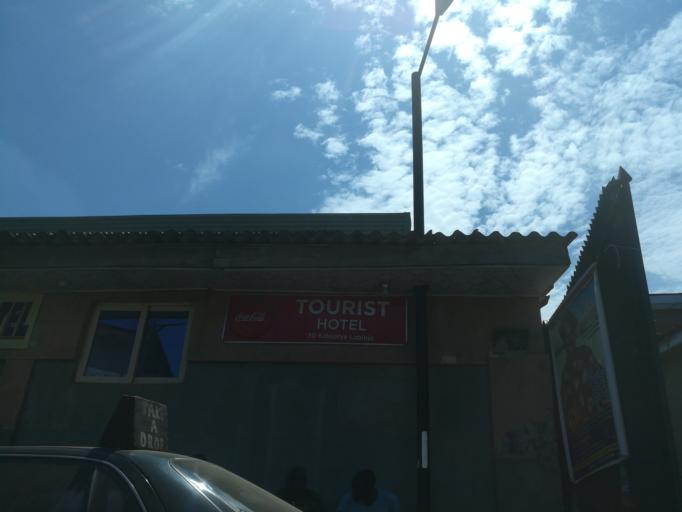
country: NG
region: Lagos
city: Oshodi
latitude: 6.5691
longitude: 3.3322
